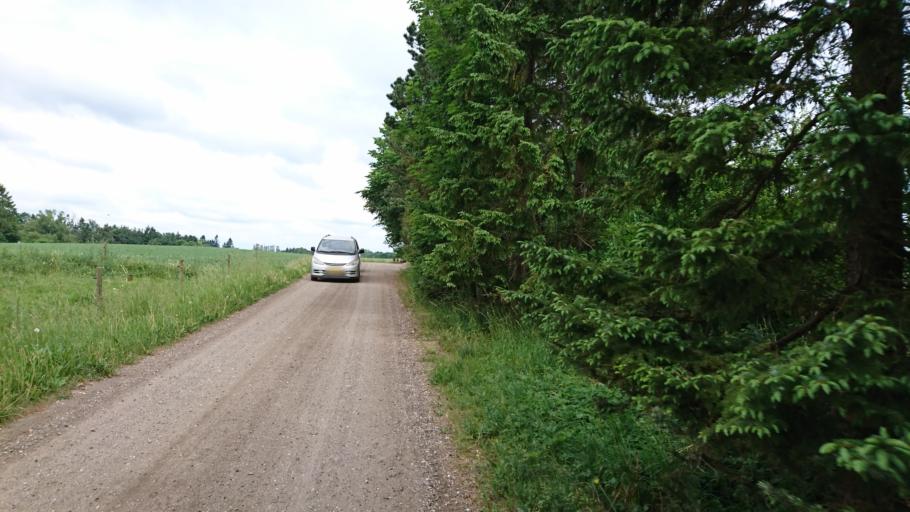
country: DK
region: Capital Region
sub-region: Ballerup Kommune
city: Malov
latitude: 55.7359
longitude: 12.3242
